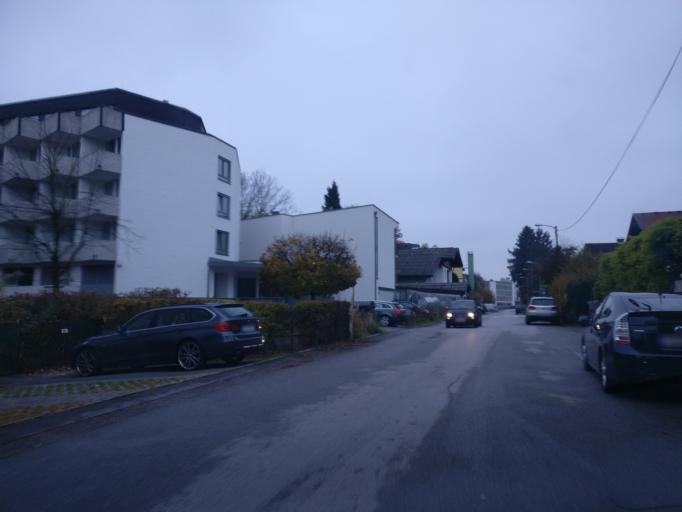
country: AT
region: Salzburg
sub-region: Salzburg Stadt
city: Salzburg
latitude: 47.7831
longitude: 13.0723
